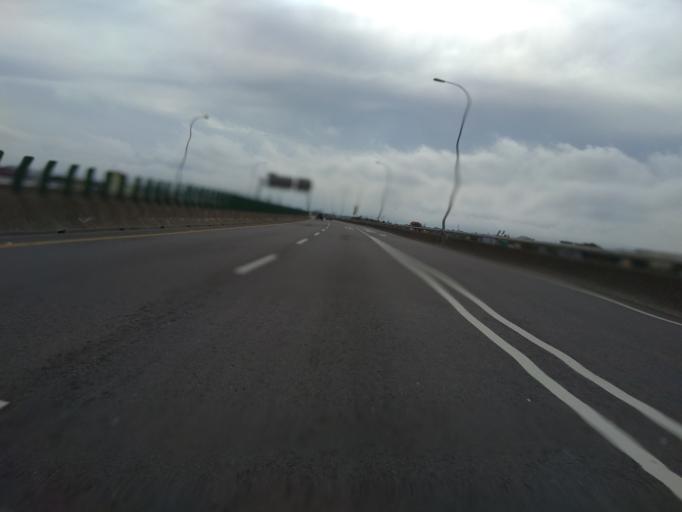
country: TW
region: Taiwan
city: Daxi
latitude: 24.9024
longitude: 121.2354
